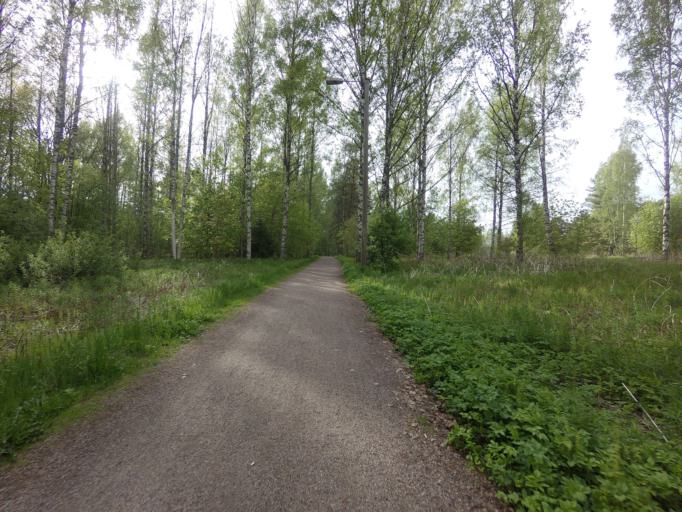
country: FI
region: Uusimaa
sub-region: Helsinki
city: Koukkuniemi
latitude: 60.1509
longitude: 24.6999
